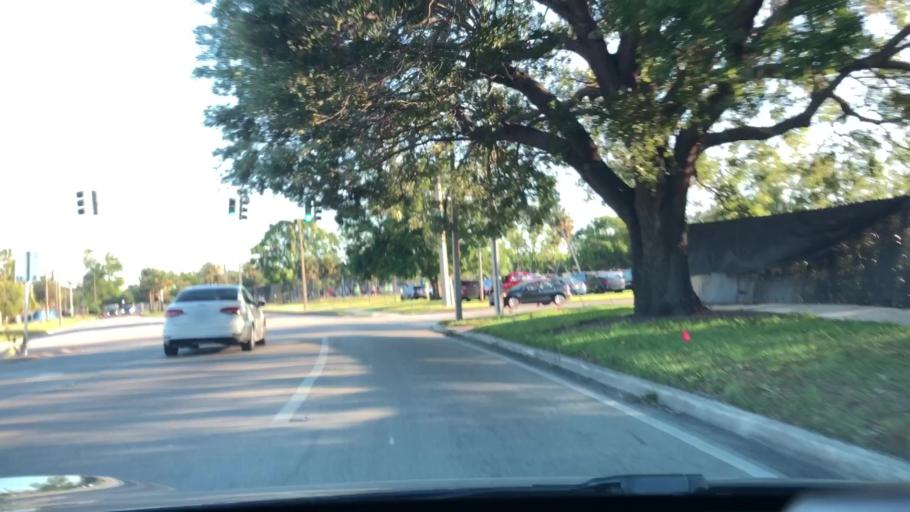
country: US
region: Florida
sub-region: Orange County
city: Orlando
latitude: 28.5498
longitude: -81.3456
